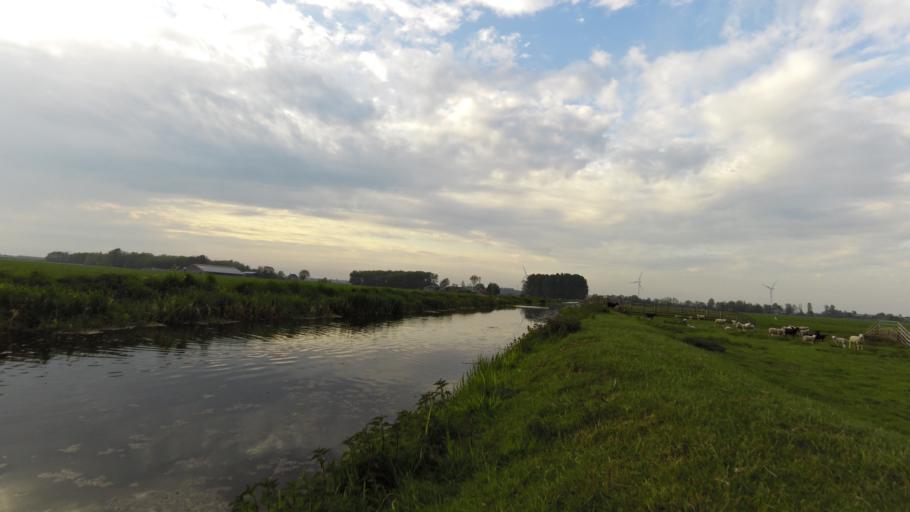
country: NL
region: South Holland
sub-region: Gemeente Alphen aan den Rijn
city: Alphen aan den Rijn
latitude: 52.1094
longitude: 4.6129
